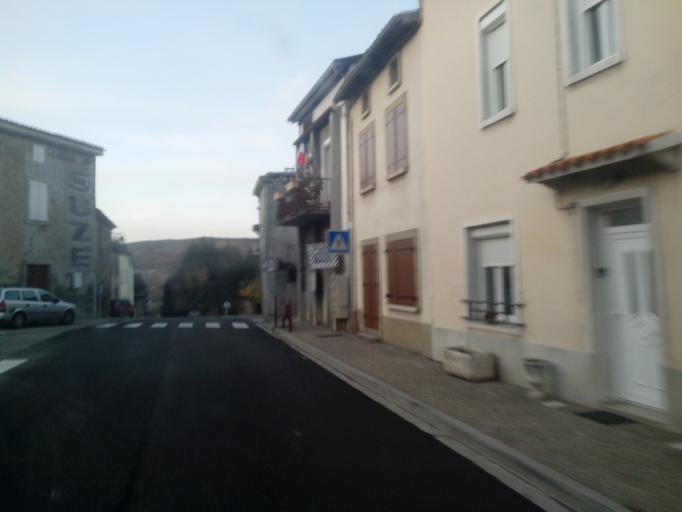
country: FR
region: Midi-Pyrenees
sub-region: Departement de l'Ariege
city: Lavelanet
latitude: 42.9170
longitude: 1.7581
